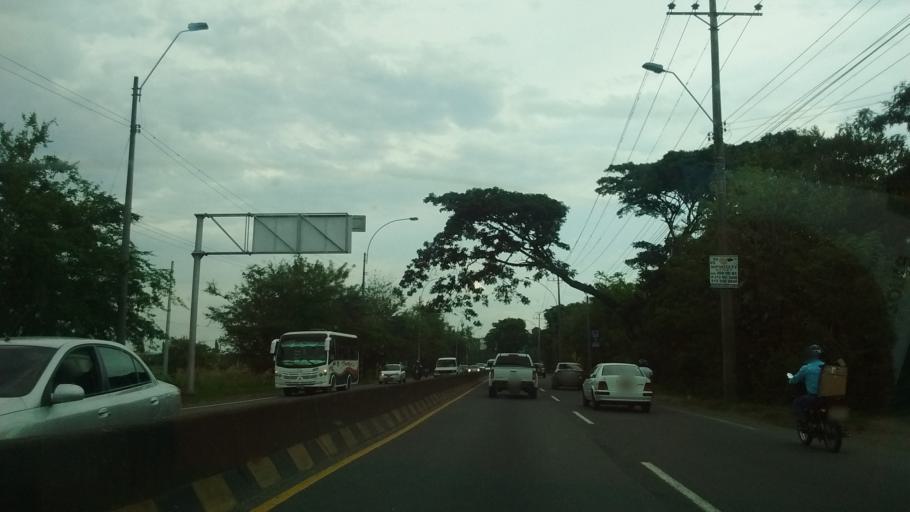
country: CO
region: Valle del Cauca
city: Cali
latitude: 3.3586
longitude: -76.5240
